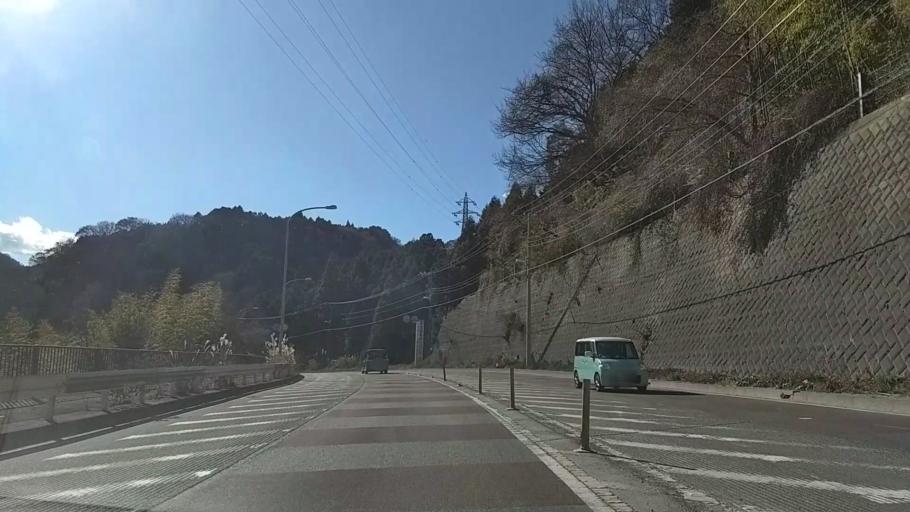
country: JP
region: Shizuoka
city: Gotemba
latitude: 35.3668
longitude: 139.0188
